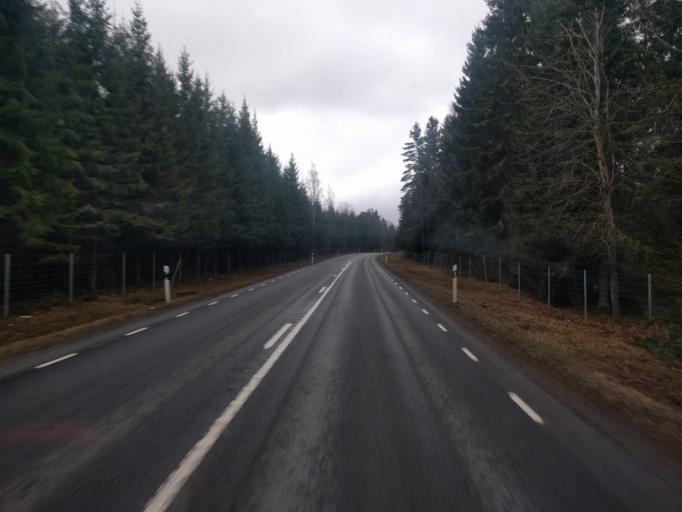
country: SE
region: Joenkoeping
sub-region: Eksjo Kommun
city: Eksjoe
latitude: 57.7002
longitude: 14.9515
